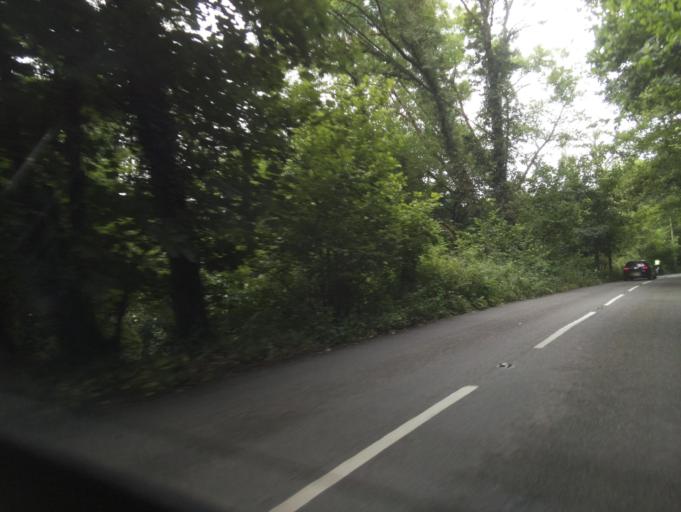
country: GB
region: England
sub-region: Devon
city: Chudleigh
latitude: 50.6476
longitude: -3.6403
